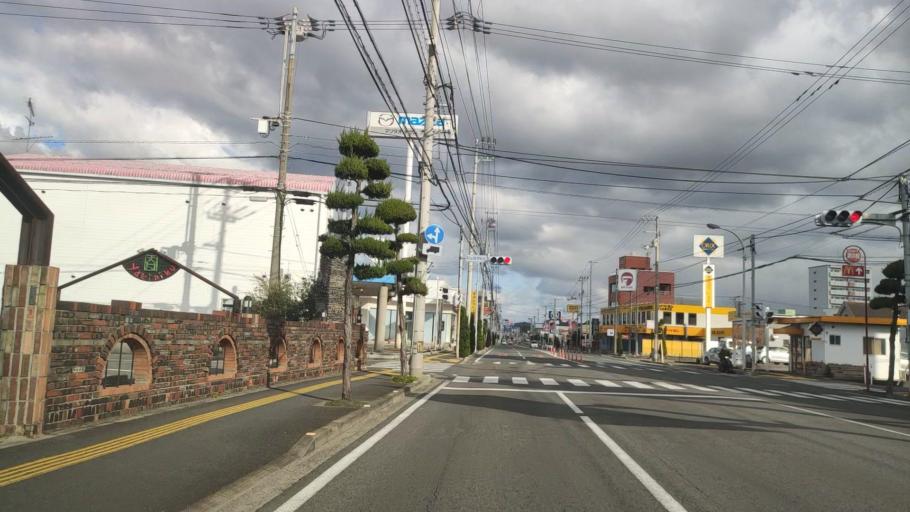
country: JP
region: Ehime
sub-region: Shikoku-chuo Shi
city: Matsuyama
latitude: 33.8577
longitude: 132.7486
